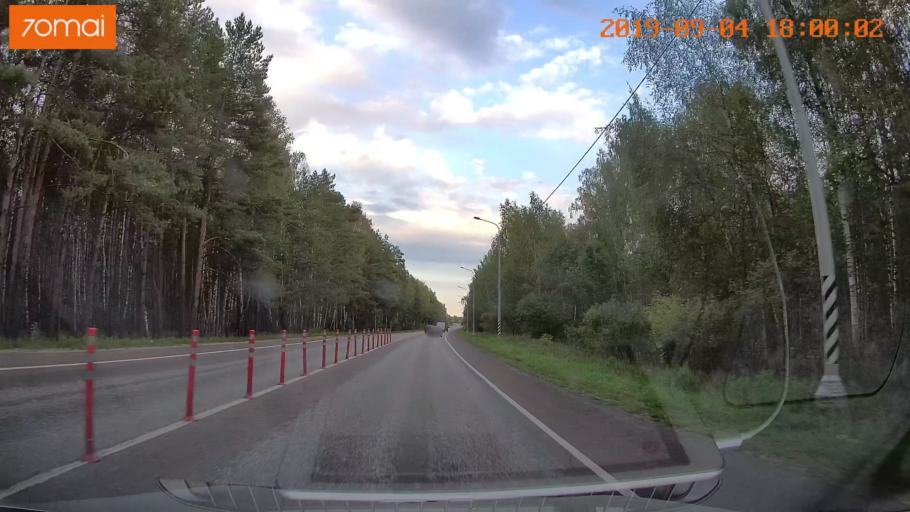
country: RU
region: Moskovskaya
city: Il'inskiy Pogost
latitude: 55.4919
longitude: 38.8540
